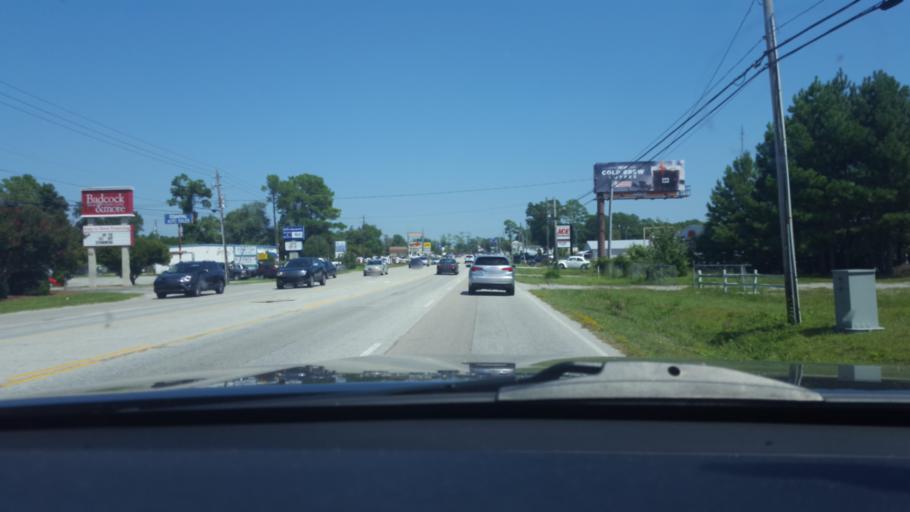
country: US
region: North Carolina
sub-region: New Hanover County
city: Ogden
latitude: 34.2585
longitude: -77.8361
